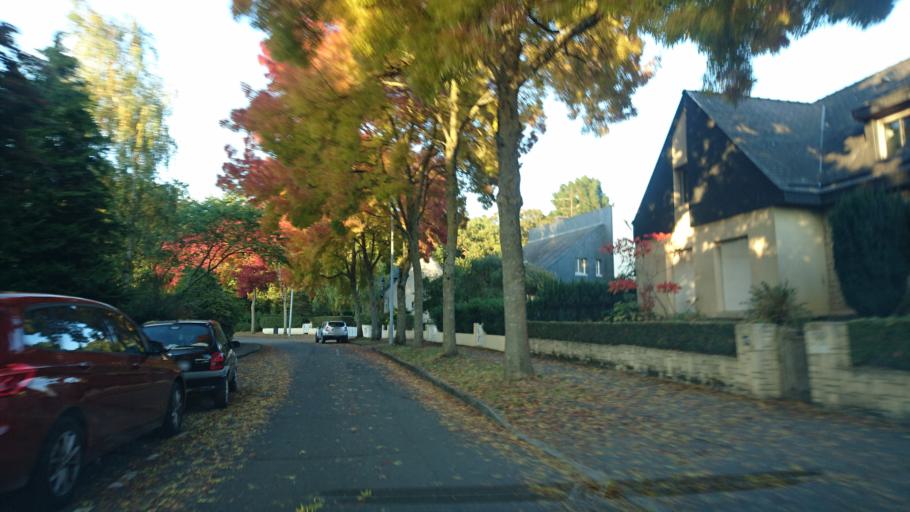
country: FR
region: Brittany
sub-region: Departement d'Ille-et-Vilaine
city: Rennes
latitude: 48.0809
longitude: -1.6892
